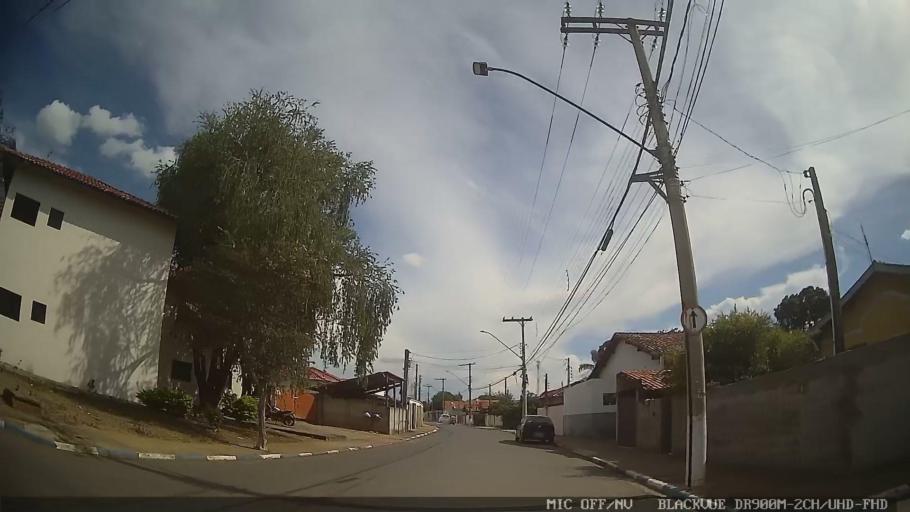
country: BR
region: Sao Paulo
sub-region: Conchas
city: Conchas
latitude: -23.0691
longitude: -47.9766
